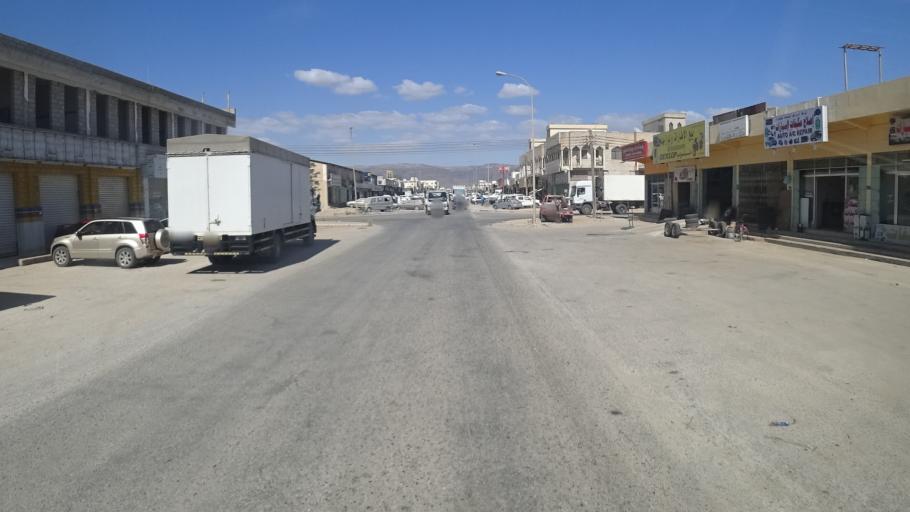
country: OM
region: Zufar
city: Salalah
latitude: 17.0161
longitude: 54.0544
